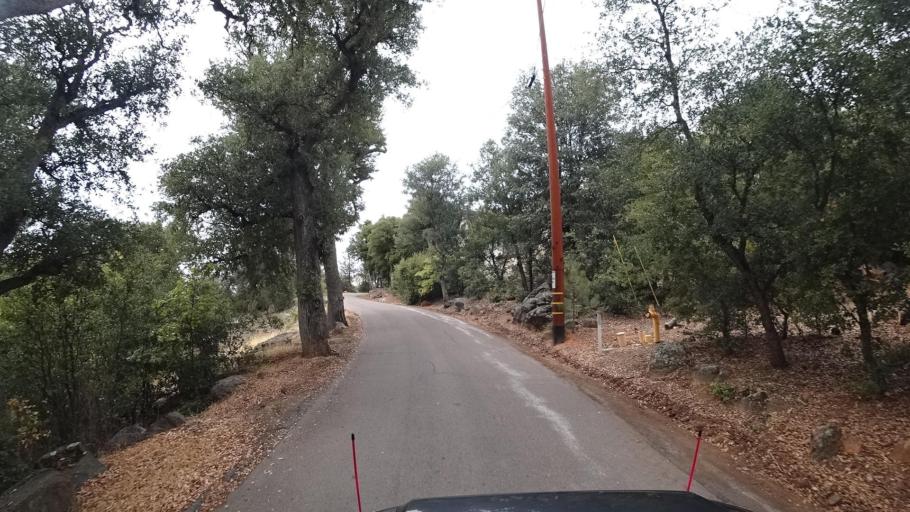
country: US
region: California
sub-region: San Diego County
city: Julian
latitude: 33.0459
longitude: -116.6257
